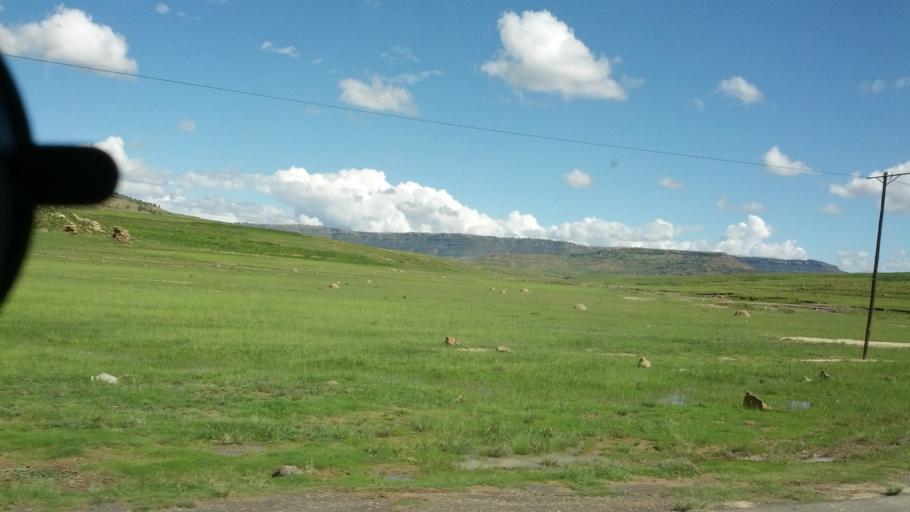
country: LS
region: Maseru
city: Maseru
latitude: -29.5498
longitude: 27.4985
